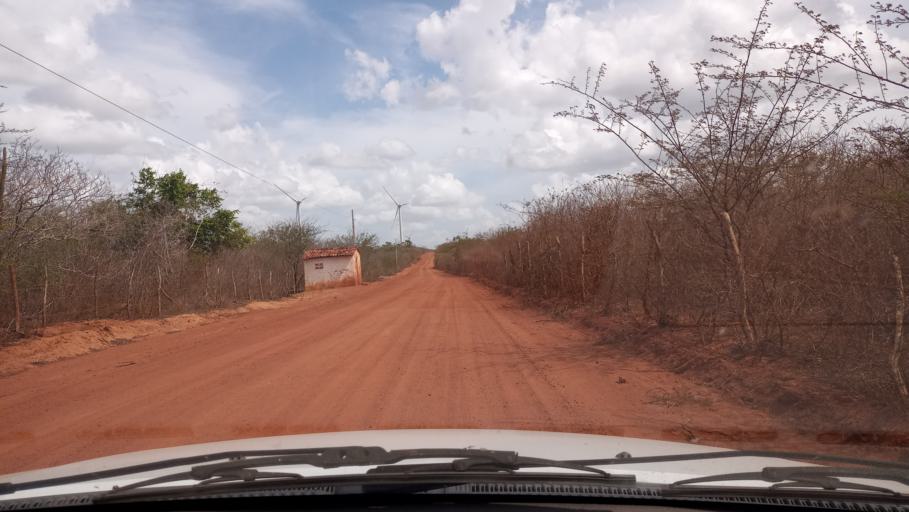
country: BR
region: Rio Grande do Norte
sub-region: Joao Camara
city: Joao Camara
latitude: -5.3837
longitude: -35.8664
